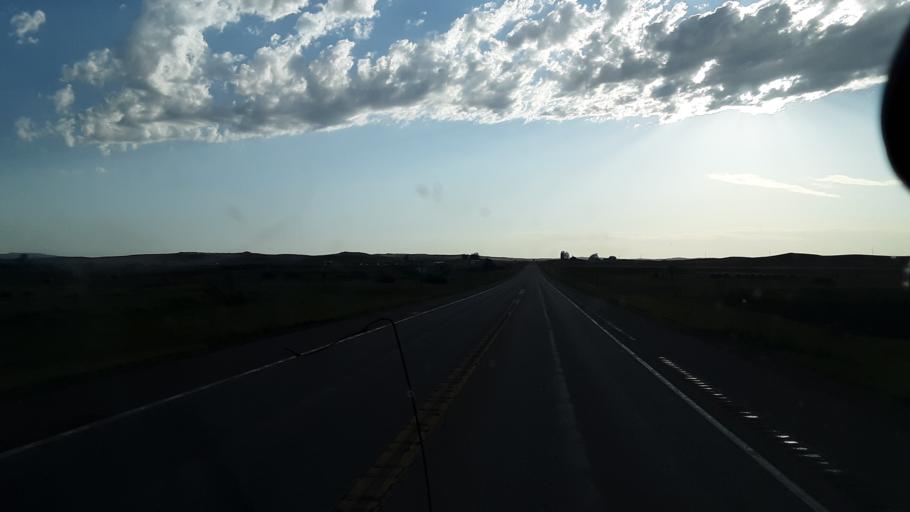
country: US
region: Montana
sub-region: Rosebud County
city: Lame Deer
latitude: 45.5284
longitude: -106.9640
